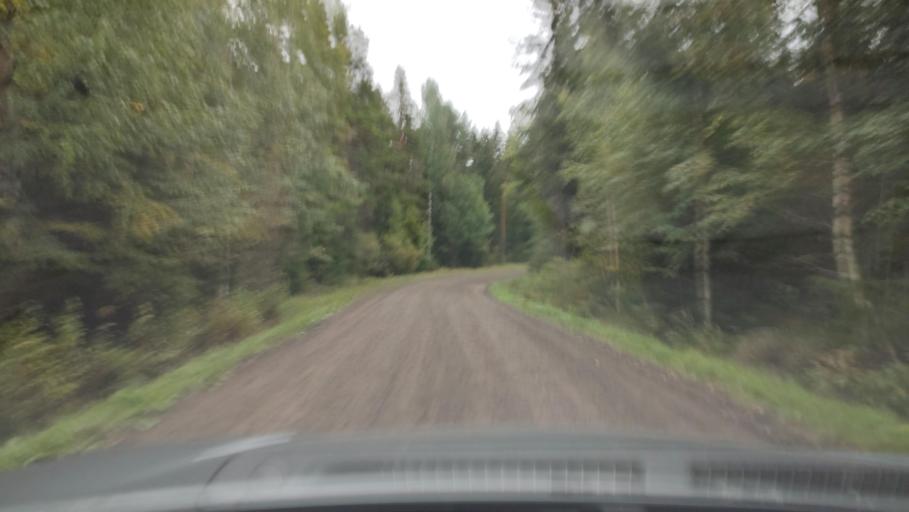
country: FI
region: Southern Ostrobothnia
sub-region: Suupohja
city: Karijoki
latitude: 62.2321
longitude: 21.5722
